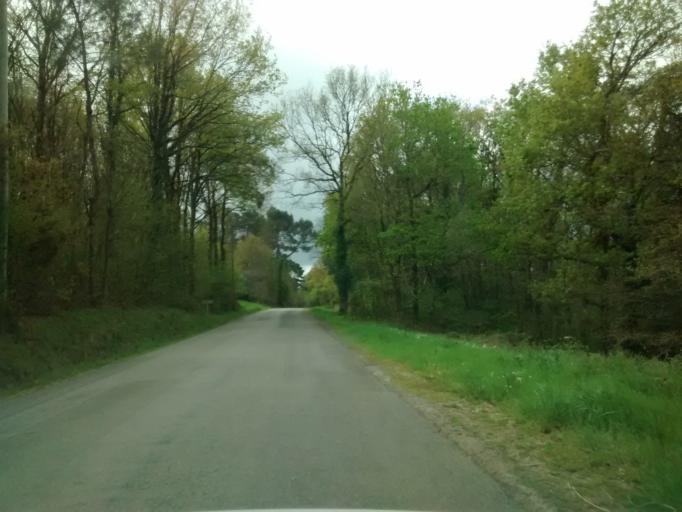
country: FR
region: Brittany
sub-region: Departement du Morbihan
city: Ruffiac
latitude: 47.7785
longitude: -2.3131
